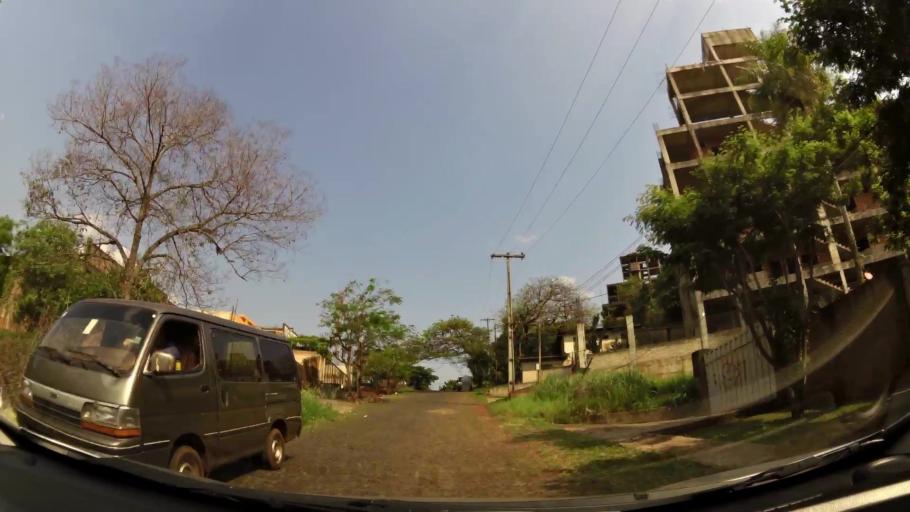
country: PY
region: Alto Parana
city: Ciudad del Este
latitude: -25.5083
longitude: -54.6244
